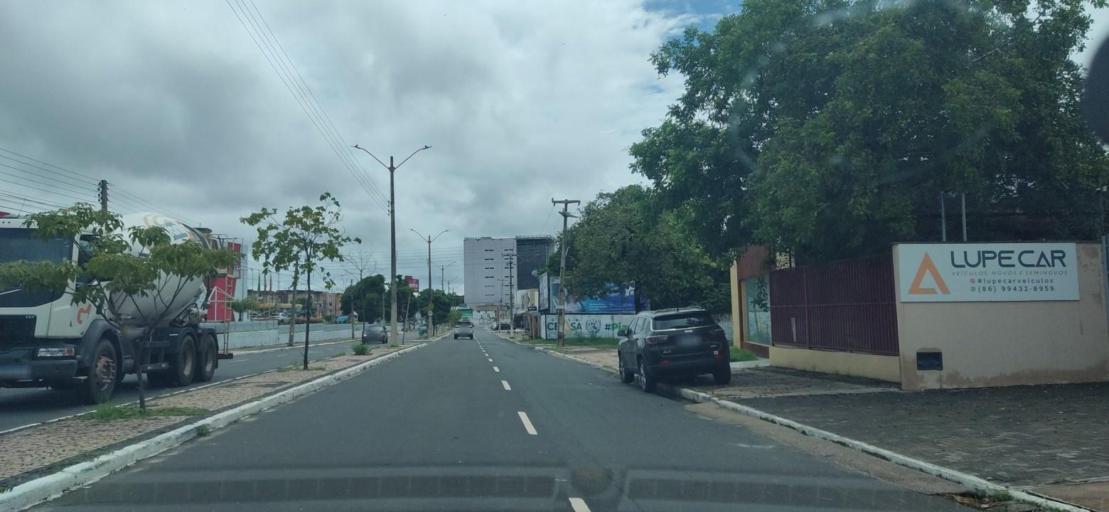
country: BR
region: Piaui
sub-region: Teresina
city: Teresina
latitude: -5.0723
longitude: -42.7745
